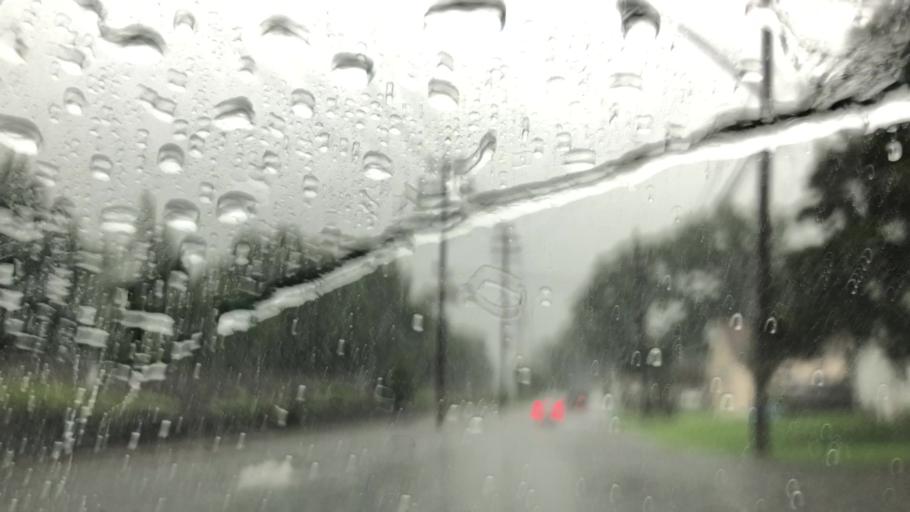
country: US
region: New Jersey
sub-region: Bergen County
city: Elmwood Park
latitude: 40.9205
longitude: -74.1147
